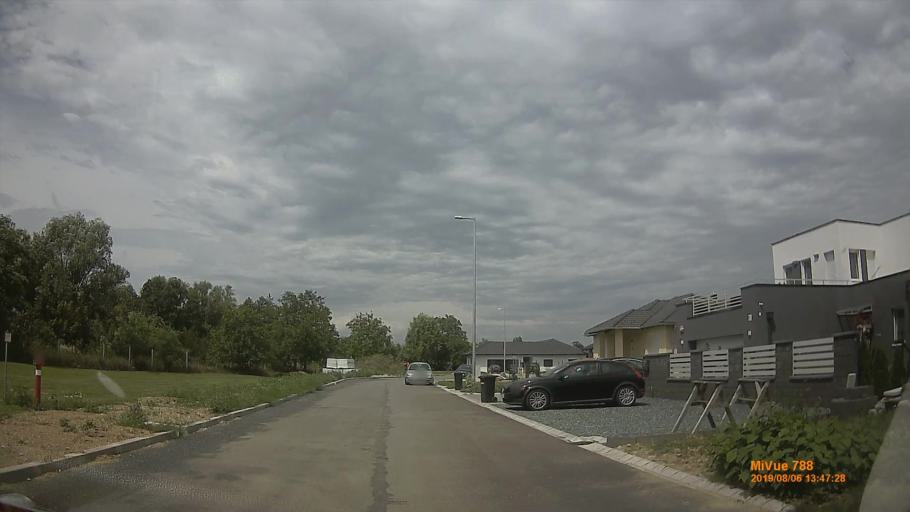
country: HU
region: Vas
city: Gencsapati
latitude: 47.2567
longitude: 16.5967
